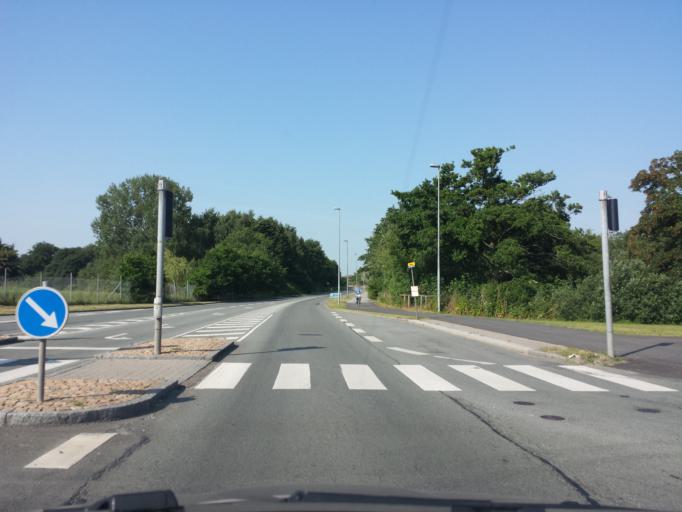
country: DK
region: Capital Region
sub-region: Ballerup Kommune
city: Malov
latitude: 55.7417
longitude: 12.3228
